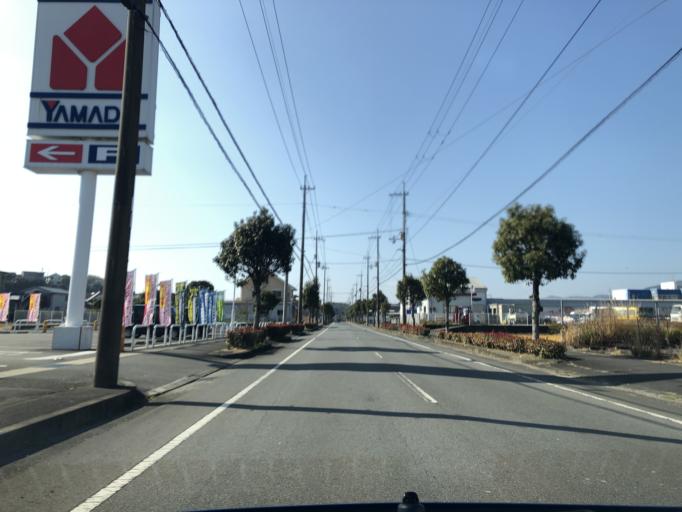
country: JP
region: Kochi
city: Sukumo
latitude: 32.9284
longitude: 132.7034
